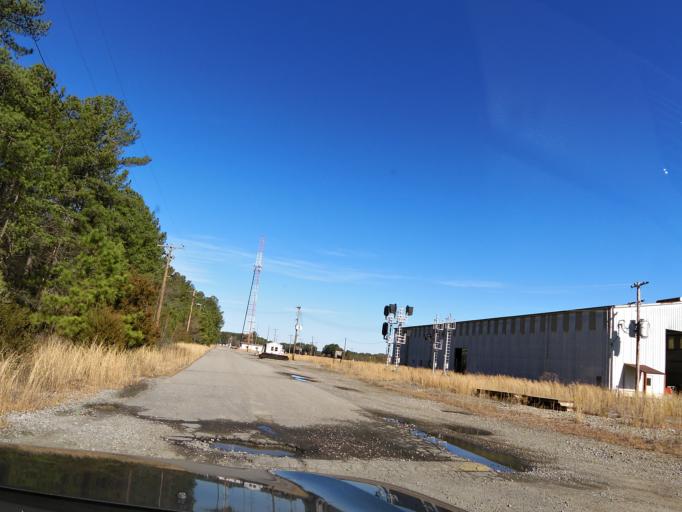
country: US
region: Virginia
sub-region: City of Petersburg
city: Petersburg
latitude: 37.1738
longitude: -77.4212
